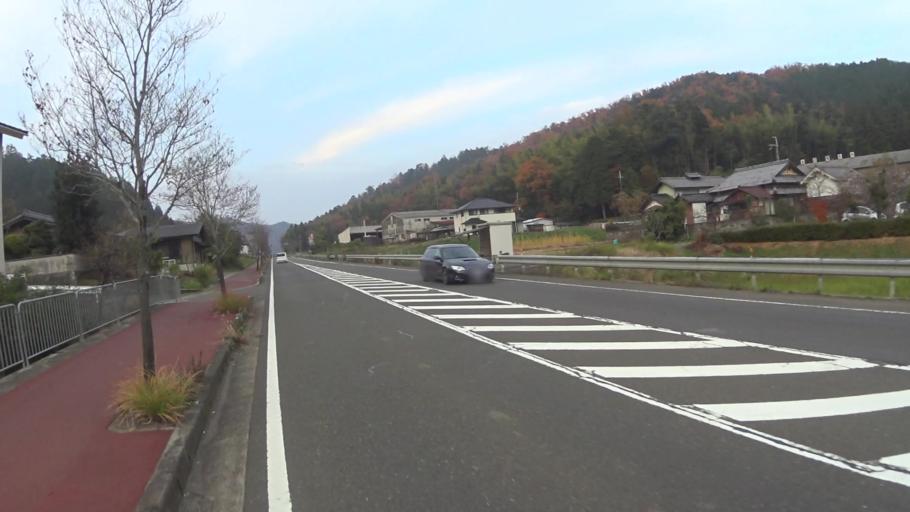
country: JP
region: Kyoto
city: Maizuru
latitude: 35.4651
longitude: 135.4226
